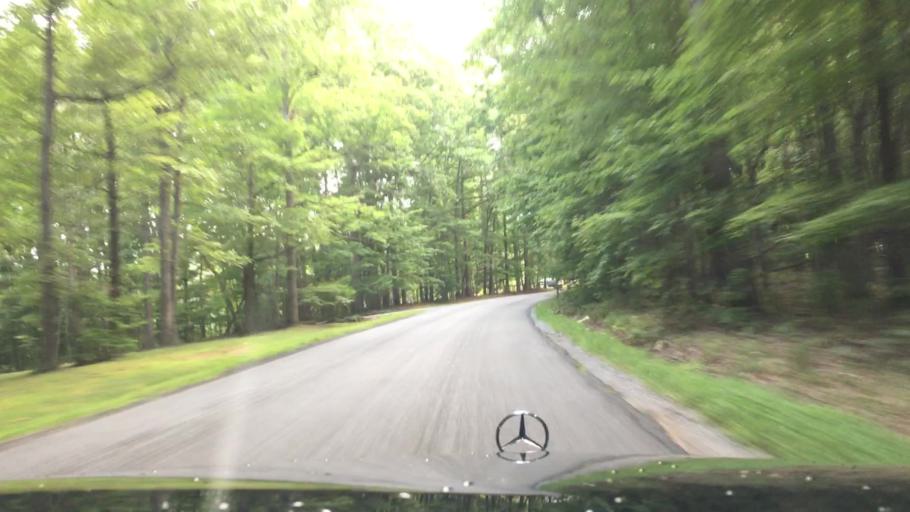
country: US
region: Virginia
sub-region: Campbell County
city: Timberlake
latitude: 37.2679
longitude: -79.3120
